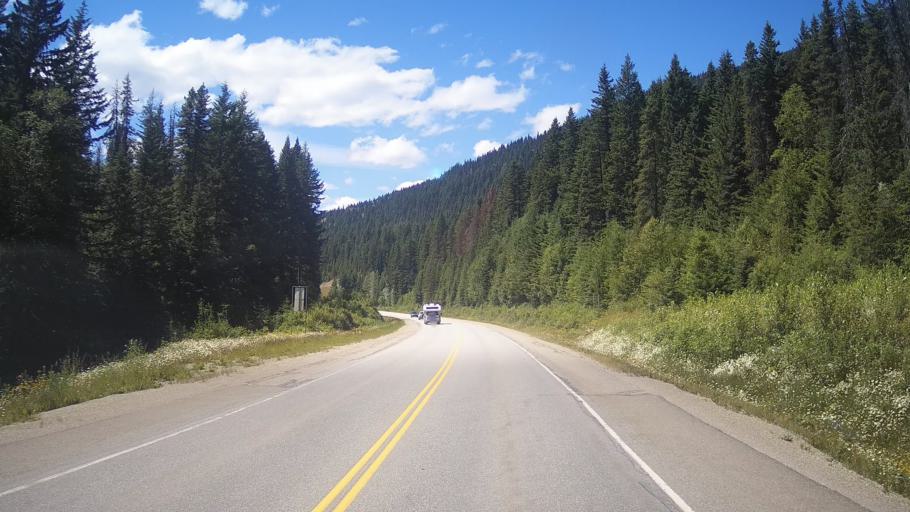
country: CA
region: Alberta
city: Grande Cache
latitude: 53.0199
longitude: -119.0983
